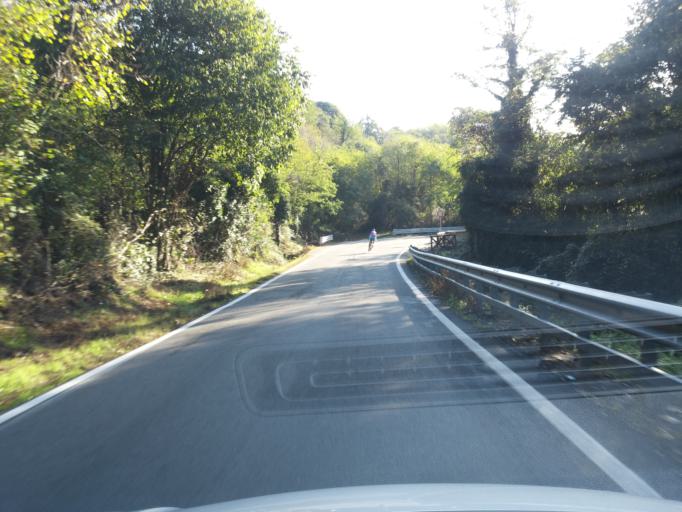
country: IT
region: Piedmont
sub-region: Provincia di Torino
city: Villareggia
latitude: 45.3025
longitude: 7.9663
